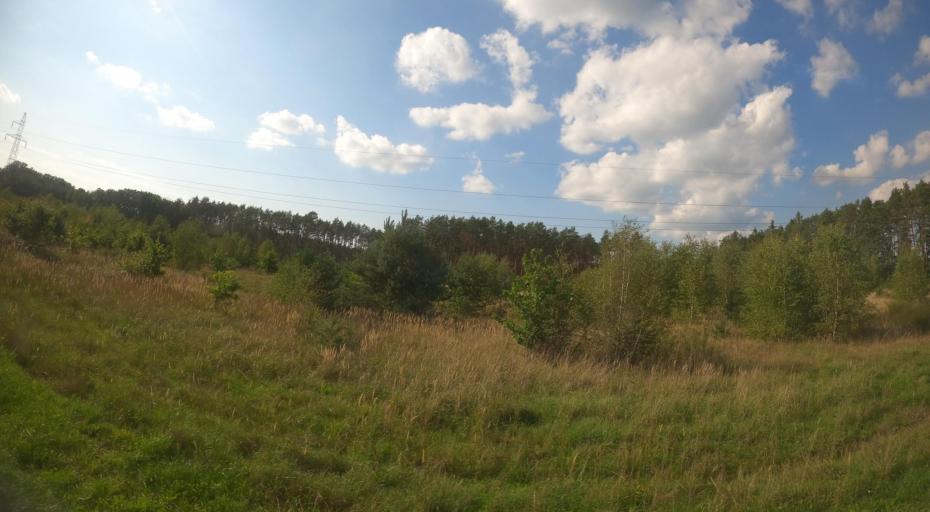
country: PL
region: Lubusz
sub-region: Powiat zielonogorski
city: Swidnica
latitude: 51.9032
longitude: 15.3183
